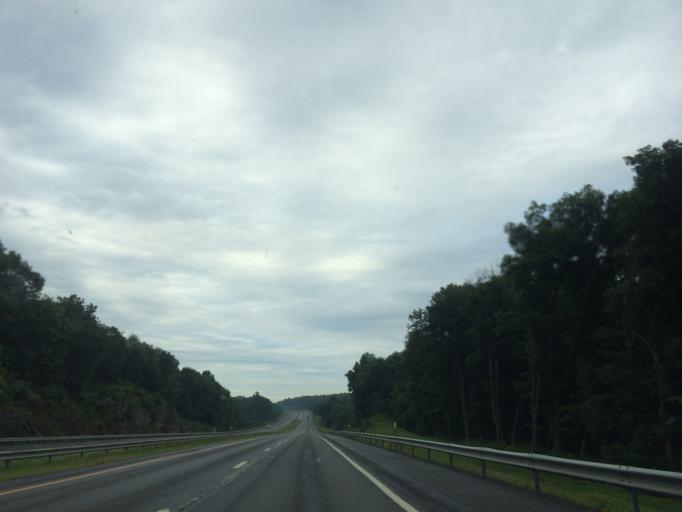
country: US
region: New York
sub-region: Greene County
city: Coxsackie
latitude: 42.3142
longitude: -73.8684
